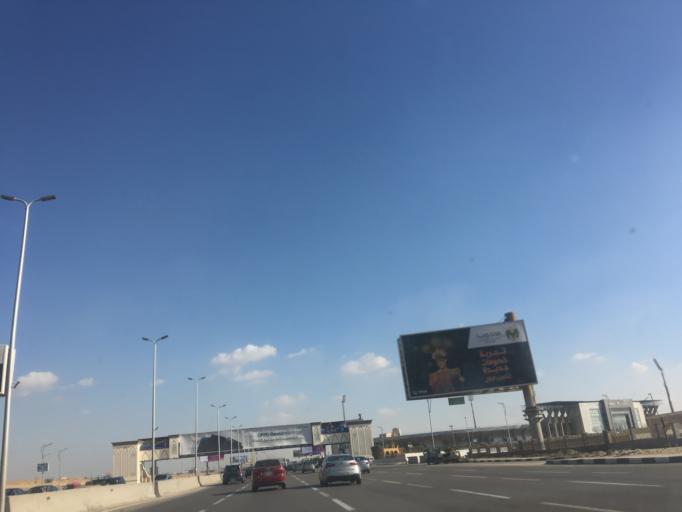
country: EG
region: Muhafazat al Qahirah
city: Cairo
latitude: 30.0226
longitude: 31.3697
